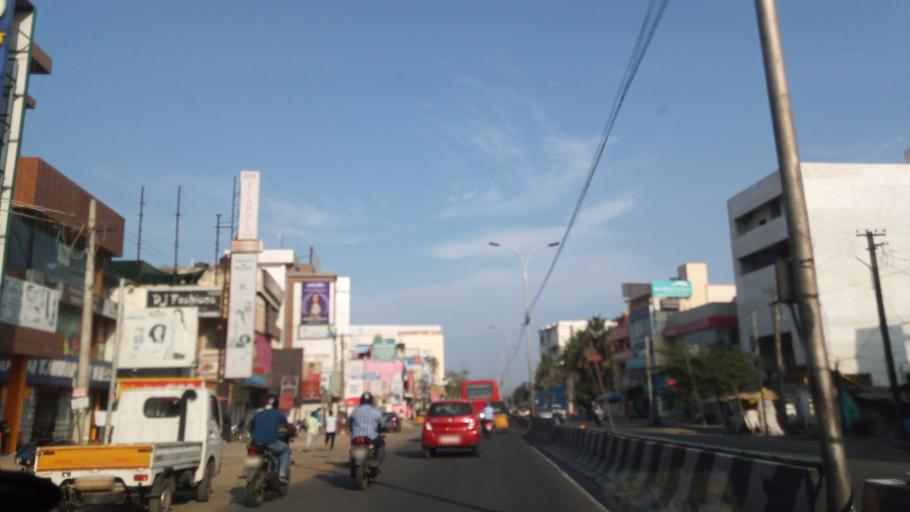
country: IN
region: Tamil Nadu
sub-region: Thiruvallur
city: Porur
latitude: 13.0337
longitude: 80.1611
